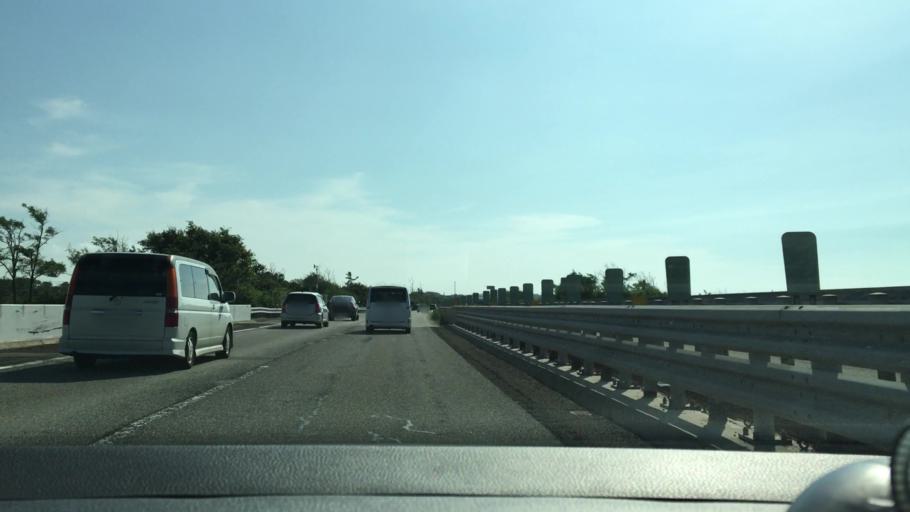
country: JP
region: Ishikawa
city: Komatsu
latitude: 36.3645
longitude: 136.3483
